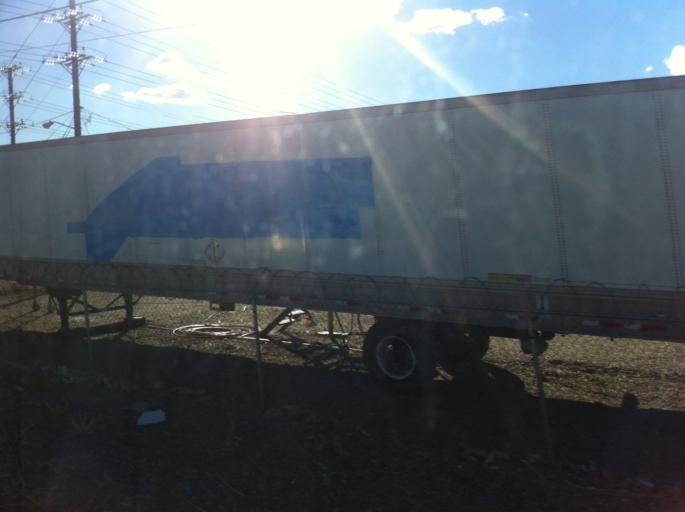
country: MX
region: Sonora
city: Hermosillo
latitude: 29.1085
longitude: -110.9125
